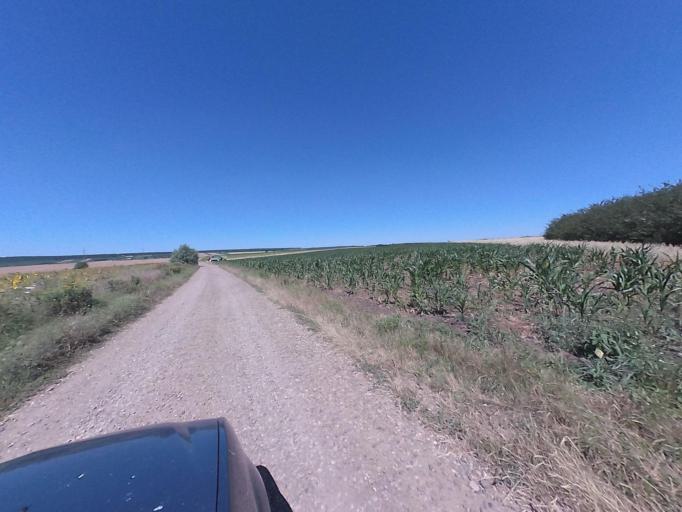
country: RO
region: Vaslui
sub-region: Comuna Costesti
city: Costesti
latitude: 46.4798
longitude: 27.7839
